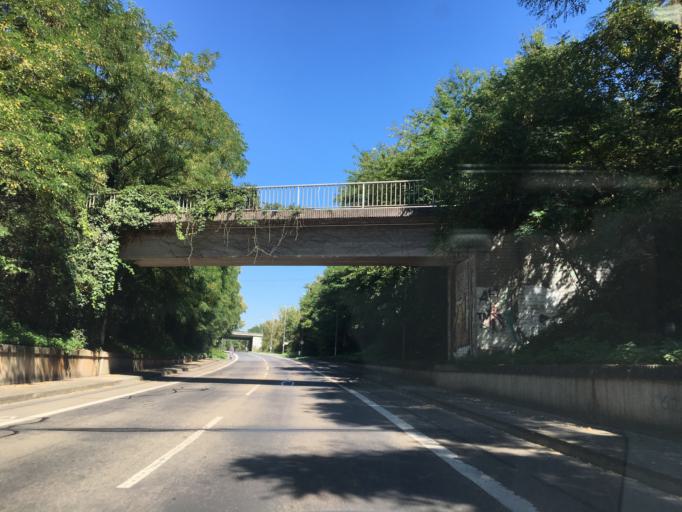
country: DE
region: Hesse
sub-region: Regierungsbezirk Darmstadt
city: Russelsheim
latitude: 49.9716
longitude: 8.3973
